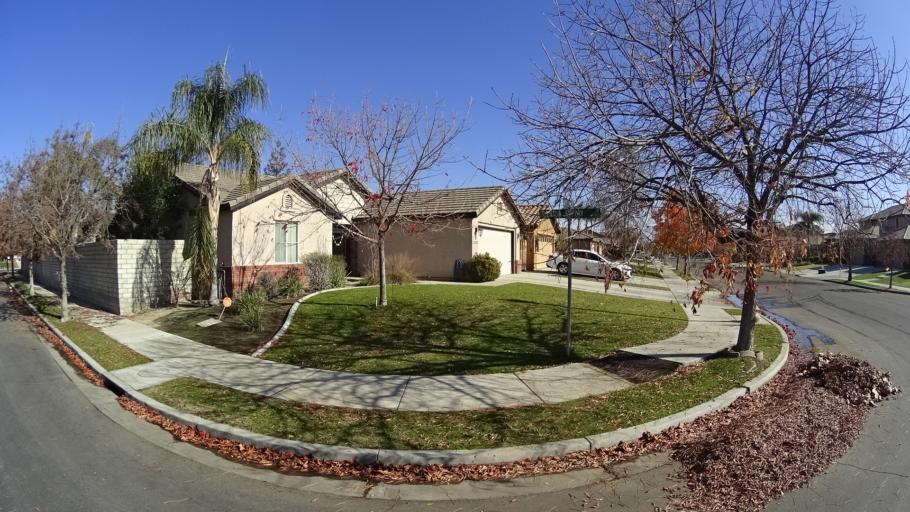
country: US
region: California
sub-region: Kern County
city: Rosedale
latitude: 35.3628
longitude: -119.1401
